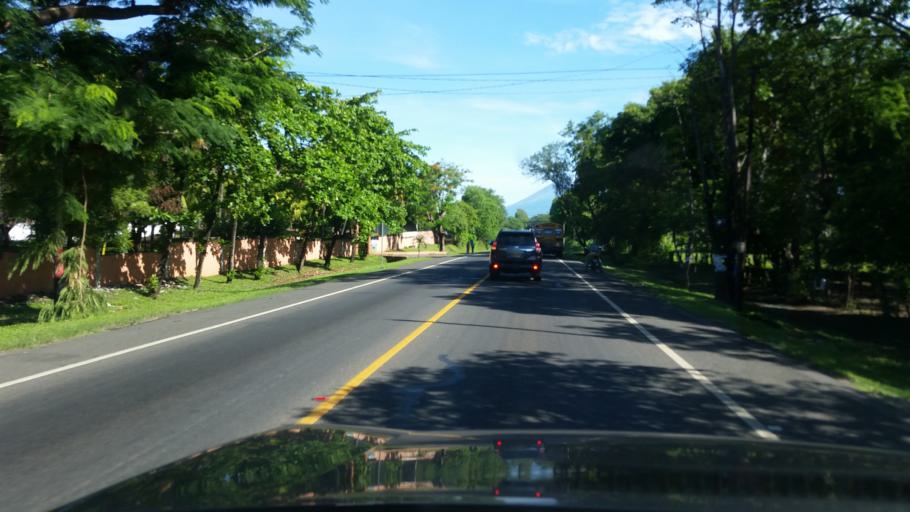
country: NI
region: Leon
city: Telica
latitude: 12.5138
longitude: -86.8621
